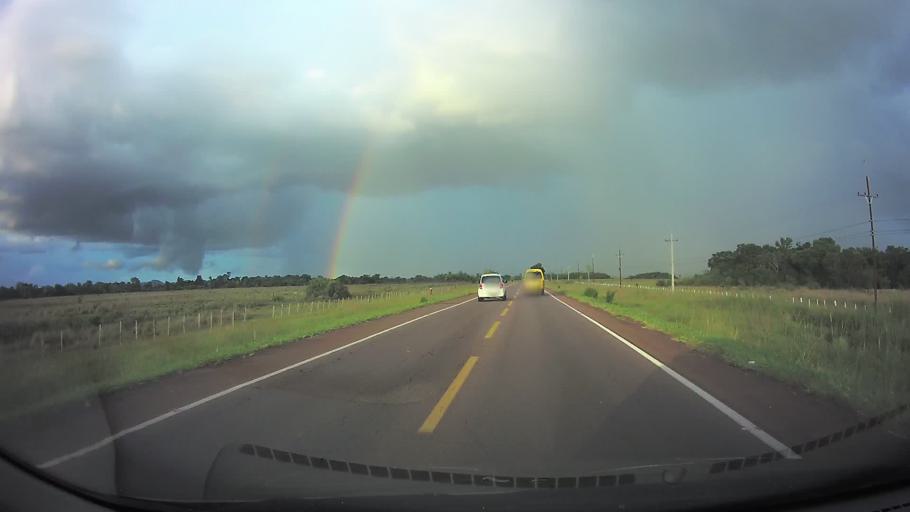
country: PY
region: Paraguari
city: Carapegua
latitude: -25.7177
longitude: -57.1975
